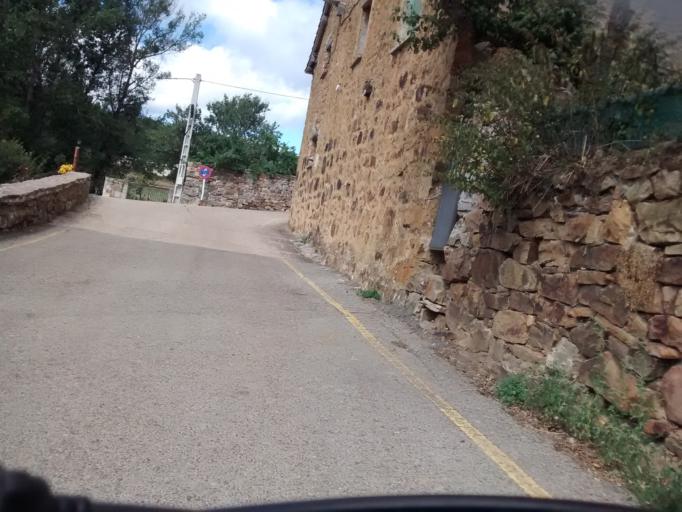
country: ES
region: Castille and Leon
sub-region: Provincia de Palencia
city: Polentinos
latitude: 42.9419
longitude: -4.4611
